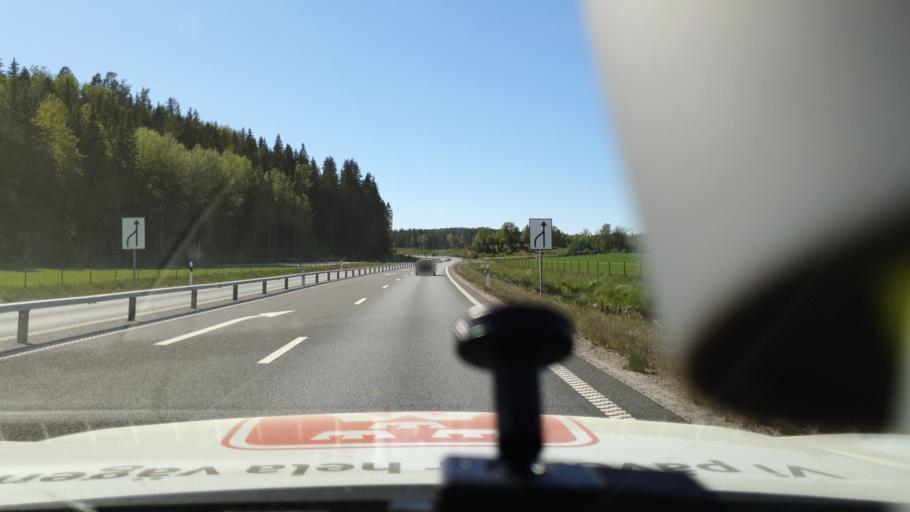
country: SE
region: Joenkoeping
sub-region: Vetlanda Kommun
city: Vetlanda
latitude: 57.4142
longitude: 15.2530
